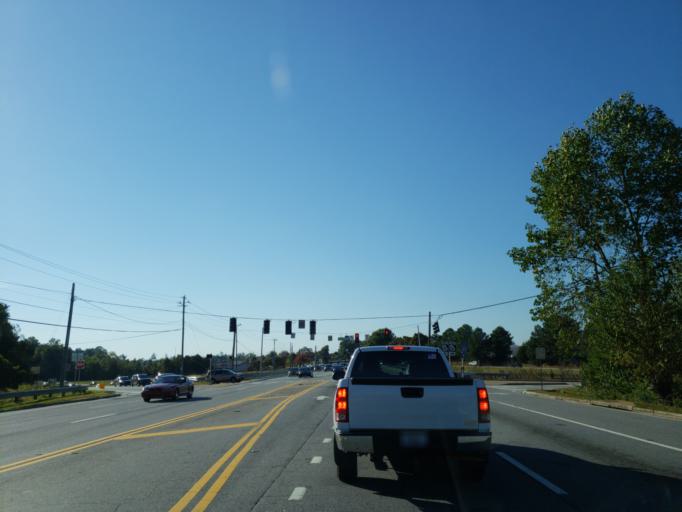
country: US
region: Georgia
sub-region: Gwinnett County
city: Lawrenceville
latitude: 33.9669
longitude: -84.0149
